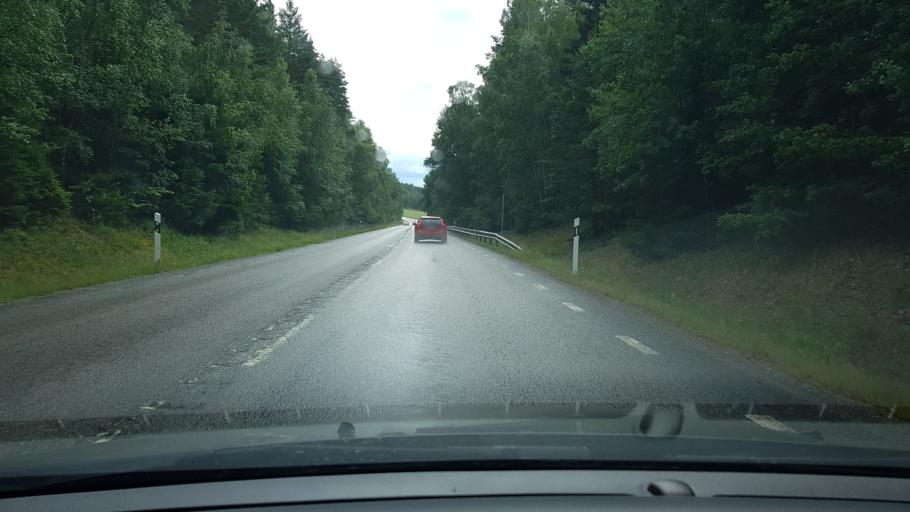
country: SE
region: Uppsala
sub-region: Uppsala Kommun
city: Saevja
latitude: 59.7892
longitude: 17.6697
